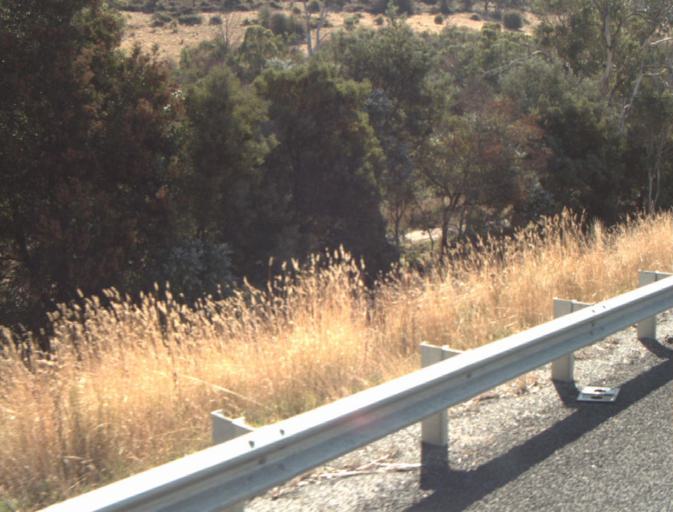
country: AU
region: Tasmania
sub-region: Launceston
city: Mayfield
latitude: -41.3635
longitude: 147.1076
